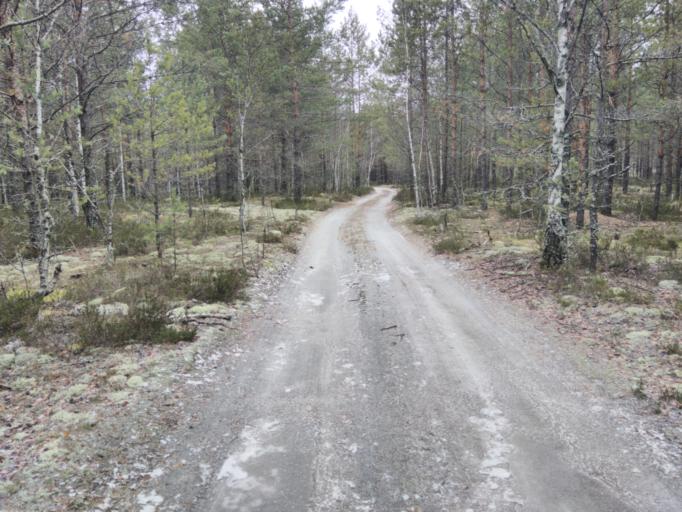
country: RU
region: Vladimir
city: Raduzhnyy
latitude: 55.9584
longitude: 40.2024
